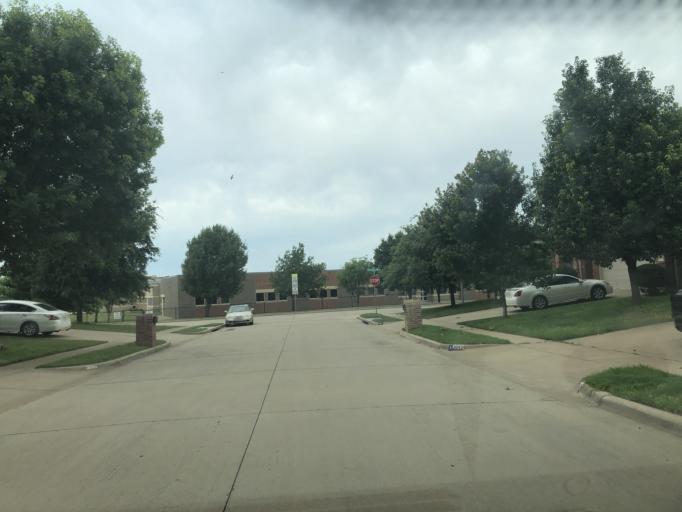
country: US
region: Texas
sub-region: Dallas County
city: Irving
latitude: 32.7984
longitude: -96.9883
